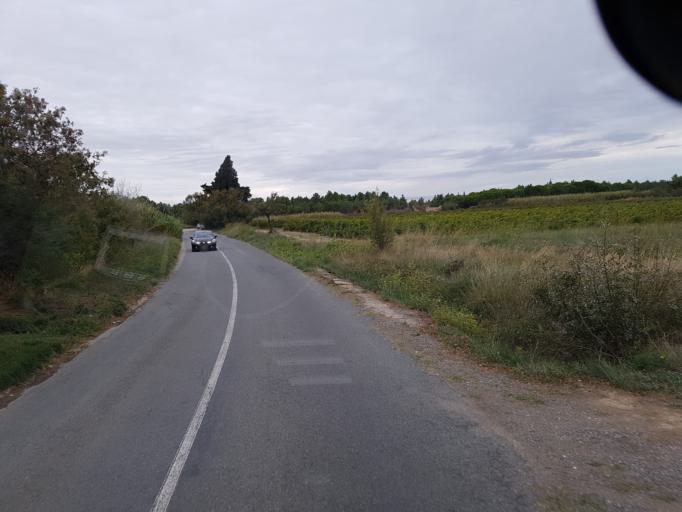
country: FR
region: Languedoc-Roussillon
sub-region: Departement de l'Aude
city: Narbonne
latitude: 43.1431
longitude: 2.9829
